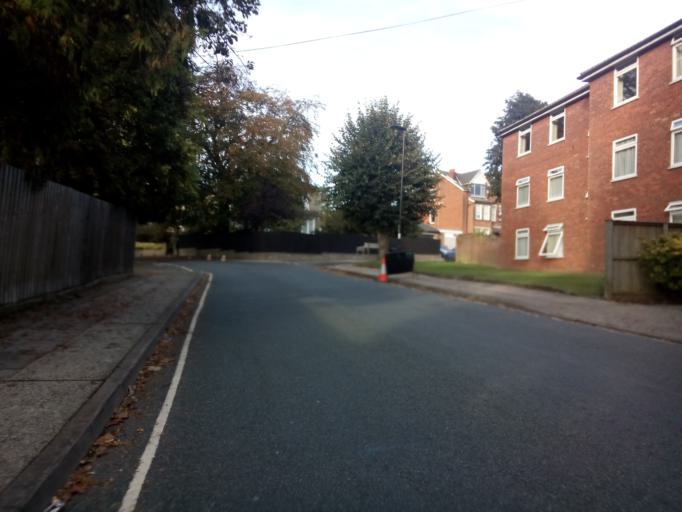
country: GB
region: England
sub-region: Suffolk
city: Ipswich
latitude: 52.0660
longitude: 1.1485
